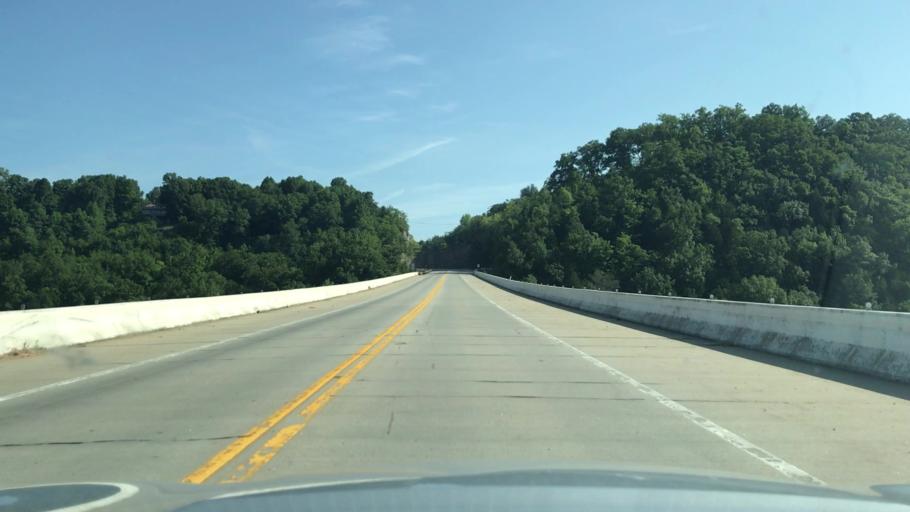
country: US
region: Tennessee
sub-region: Pickett County
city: Byrdstown
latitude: 36.5337
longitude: -85.1609
